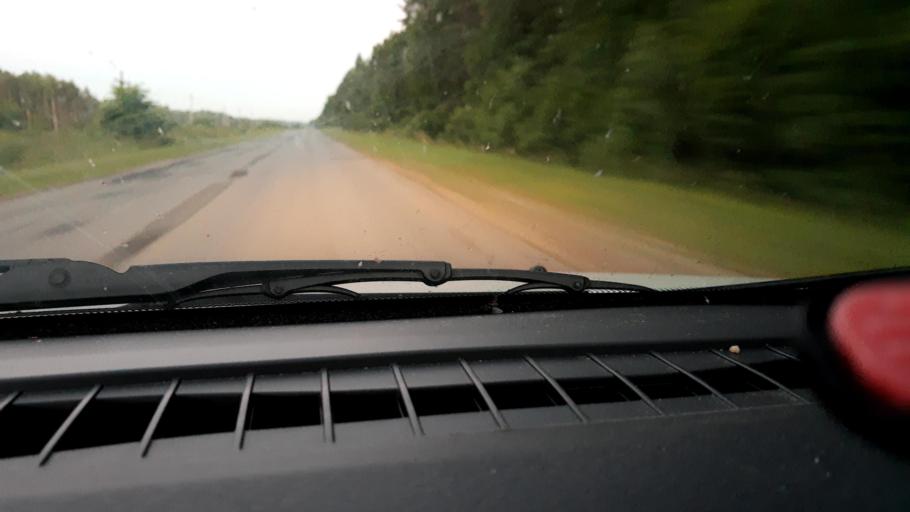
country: RU
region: Nizjnij Novgorod
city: Prudy
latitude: 57.4573
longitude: 46.0478
